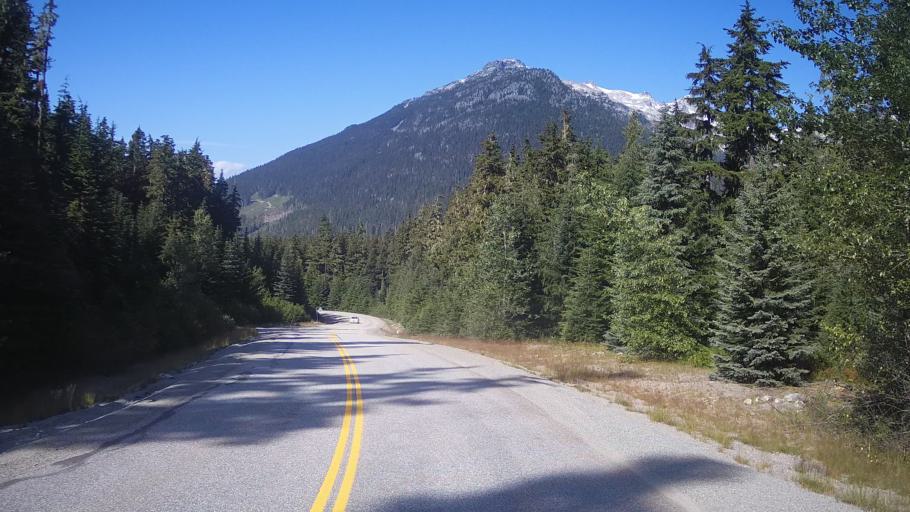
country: CA
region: British Columbia
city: Pemberton
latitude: 50.3660
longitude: -122.5183
